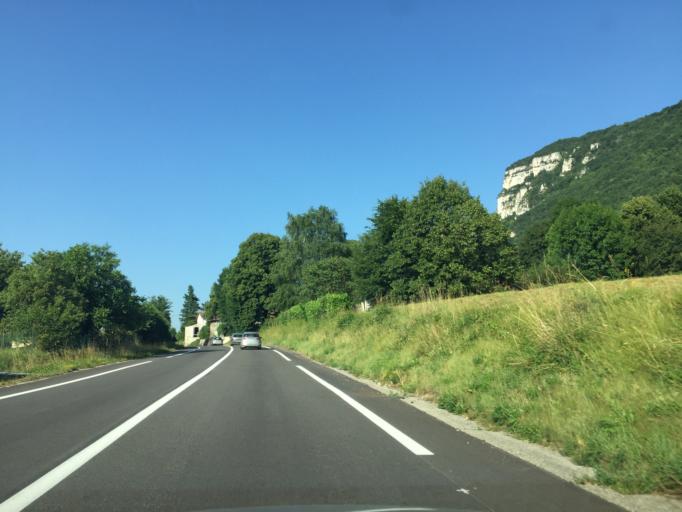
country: FR
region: Rhone-Alpes
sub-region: Departement de l'Isere
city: Saint-Sauveur
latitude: 45.1547
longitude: 5.3818
